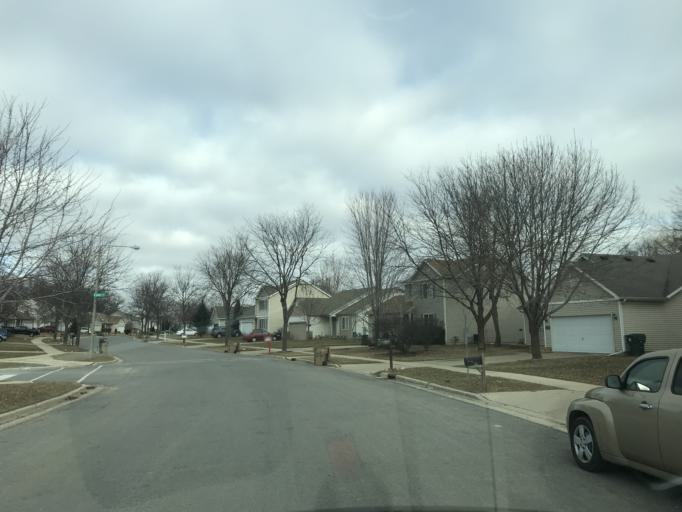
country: US
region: Wisconsin
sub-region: Dane County
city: Monona
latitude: 43.1160
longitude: -89.2892
